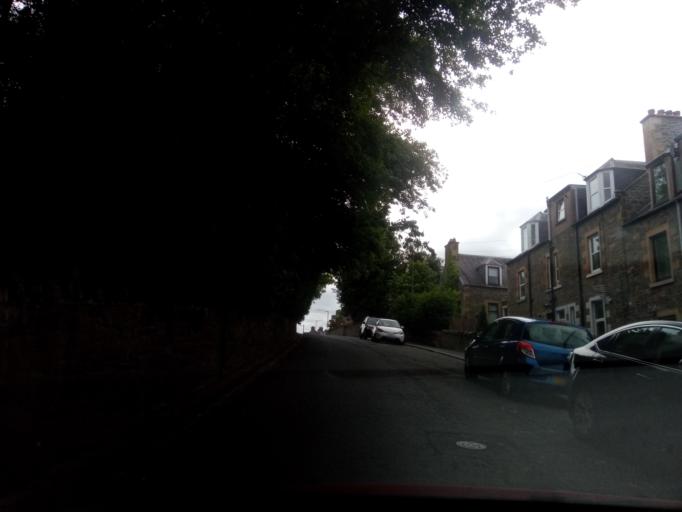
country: GB
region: Scotland
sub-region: The Scottish Borders
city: Selkirk
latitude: 55.5525
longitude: -2.8342
